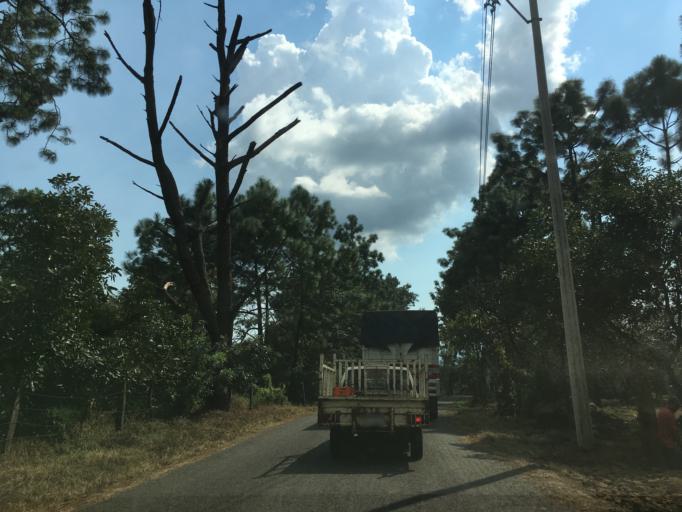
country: MX
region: Michoacan
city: Tingambato
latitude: 19.4541
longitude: -101.8663
